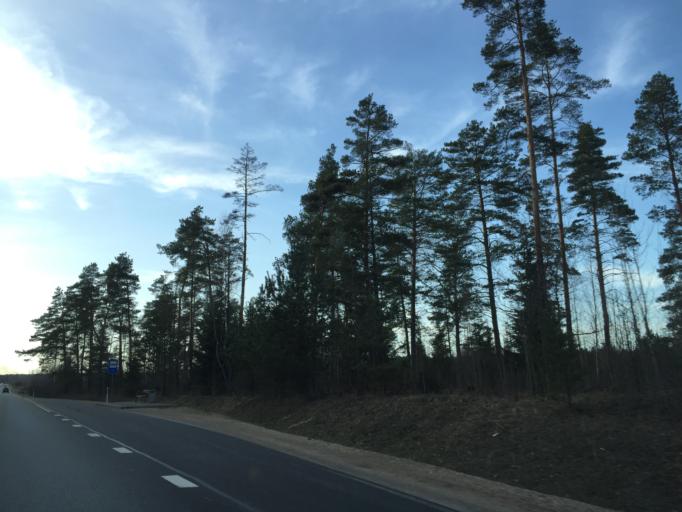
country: LV
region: Ikskile
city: Ikskile
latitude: 56.8936
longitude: 24.4469
